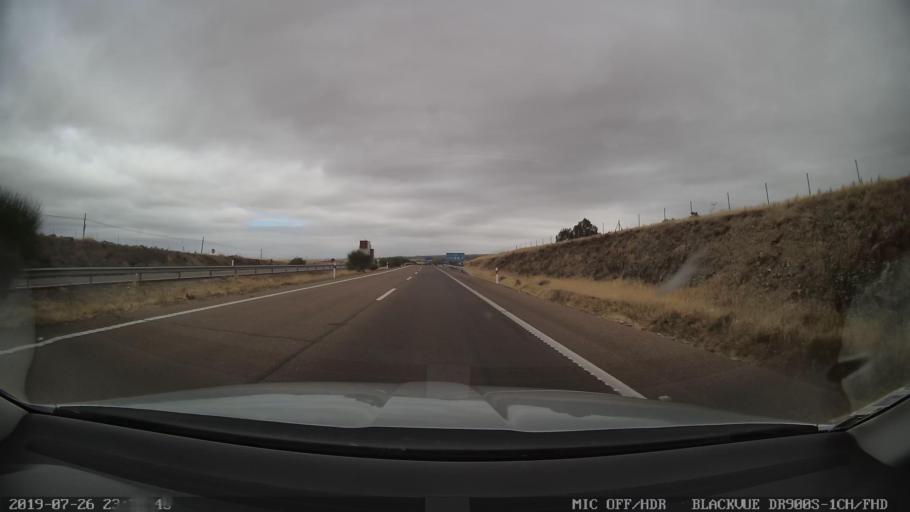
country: ES
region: Extremadura
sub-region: Provincia de Caceres
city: Trujillo
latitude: 39.3996
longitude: -5.8887
